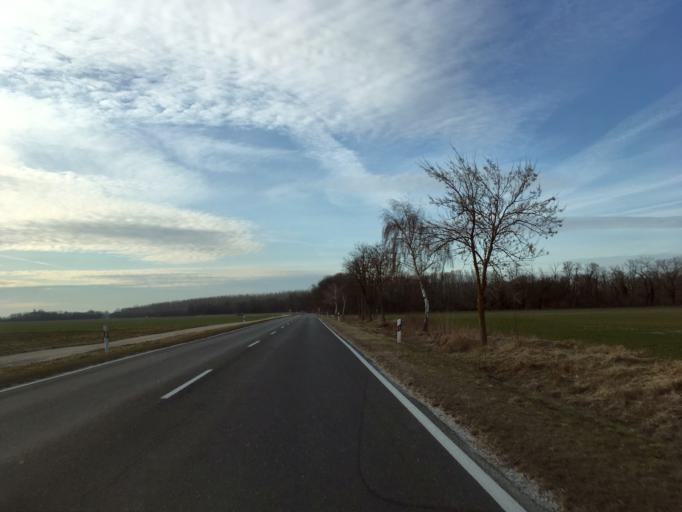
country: HU
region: Gyor-Moson-Sopron
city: Kimle
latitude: 47.8269
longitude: 17.3210
